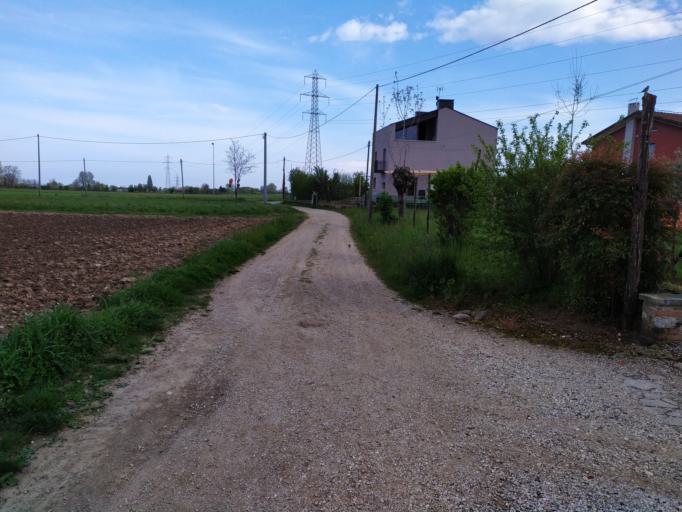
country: IT
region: Veneto
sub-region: Provincia di Vicenza
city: Giavenale
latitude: 45.6960
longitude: 11.3981
